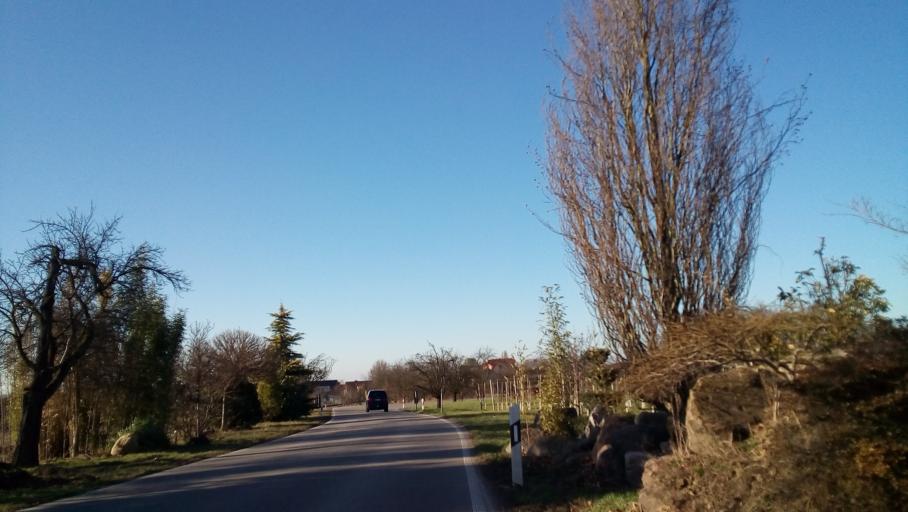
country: DE
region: Baden-Wuerttemberg
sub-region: Freiburg Region
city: Achern
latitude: 48.6081
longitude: 8.0847
